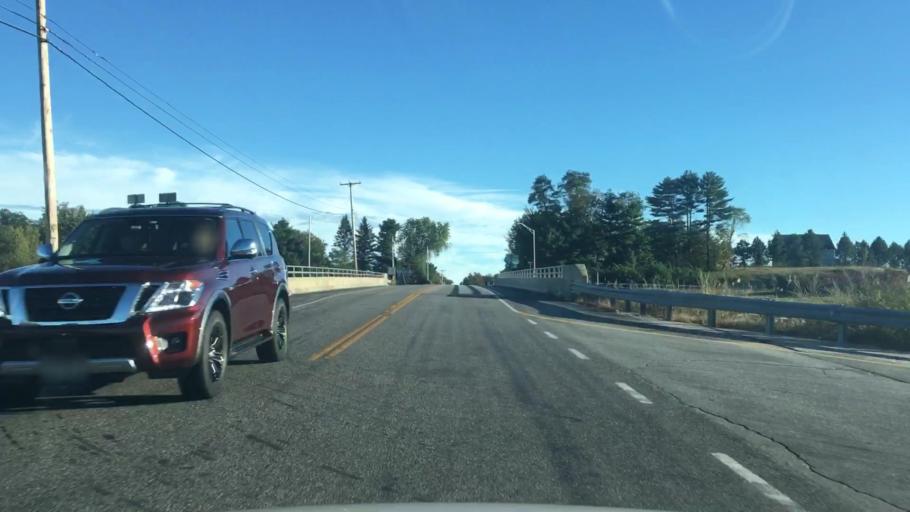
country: US
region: Maine
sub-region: Androscoggin County
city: Sabattus
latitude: 44.1017
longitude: -70.0862
